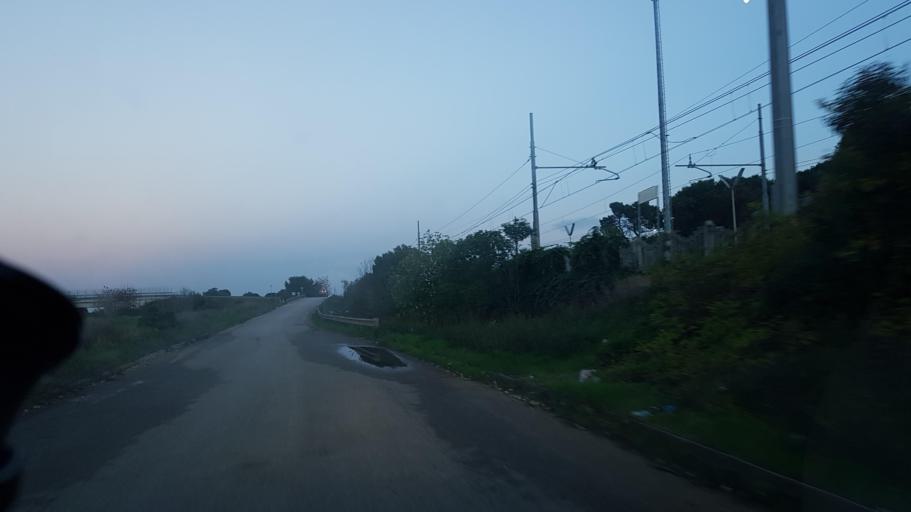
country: IT
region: Apulia
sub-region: Provincia di Brindisi
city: Latiano
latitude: 40.5581
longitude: 17.7175
